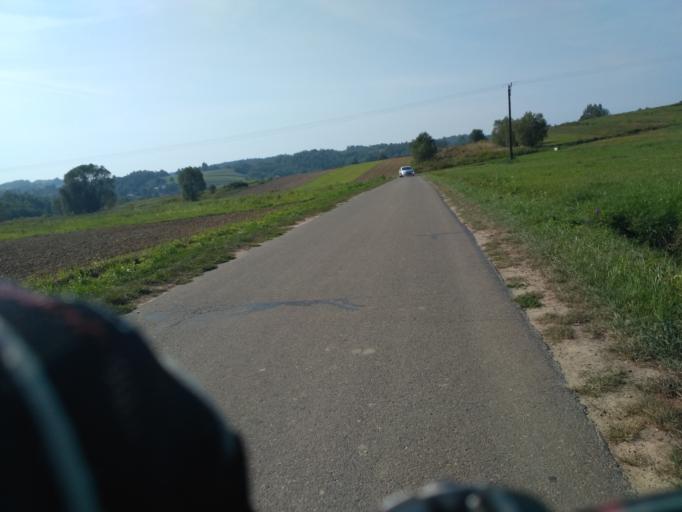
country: PL
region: Subcarpathian Voivodeship
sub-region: Powiat brzozowski
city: Golcowa
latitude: 49.7808
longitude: 22.0134
